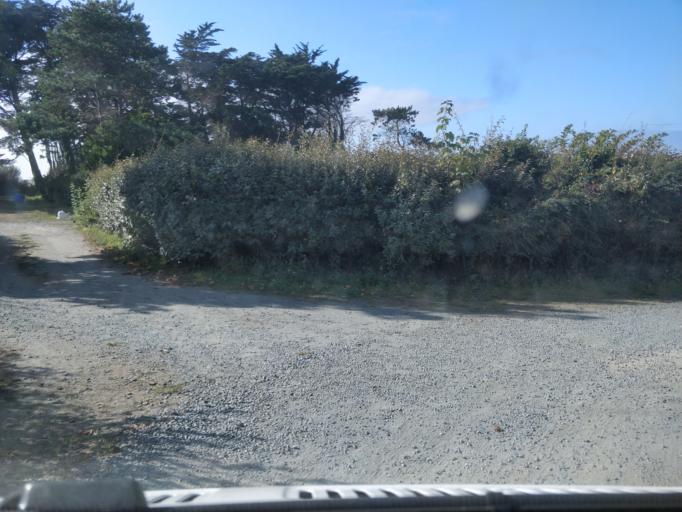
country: FR
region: Brittany
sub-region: Departement du Finistere
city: Plouhinec
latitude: 48.0060
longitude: -4.4947
